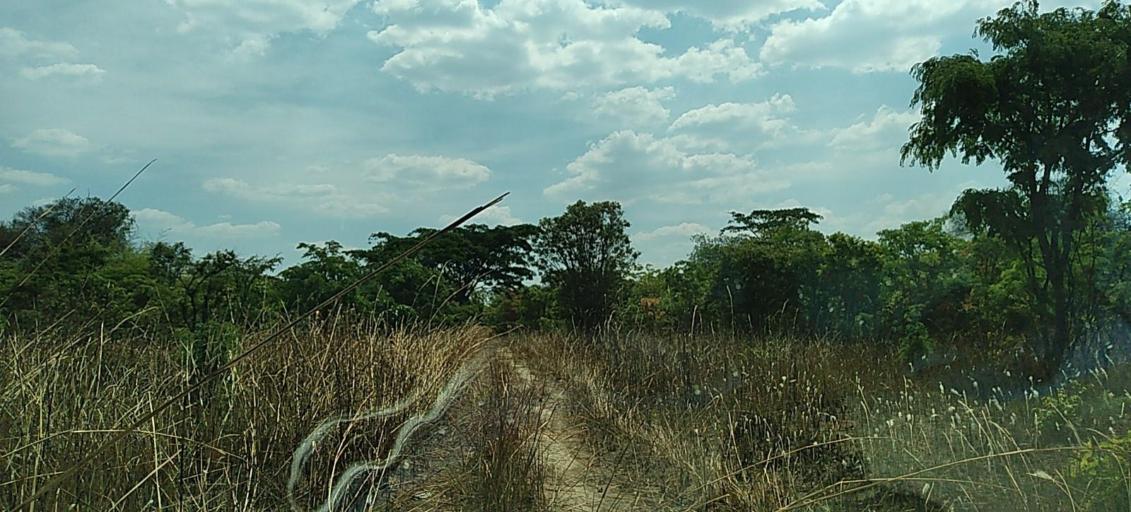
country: ZM
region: Copperbelt
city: Chililabombwe
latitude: -12.3313
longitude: 27.7651
